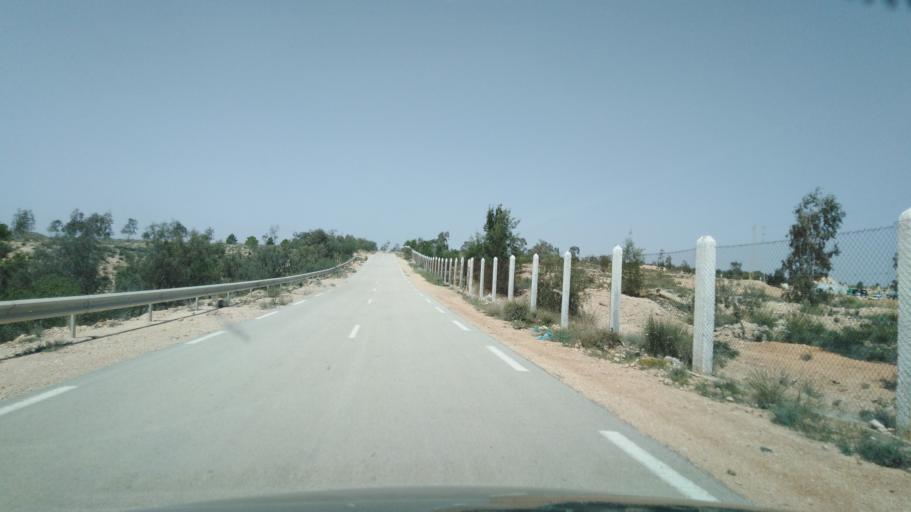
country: TN
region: Safaqis
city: Sfax
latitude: 34.7067
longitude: 10.5251
